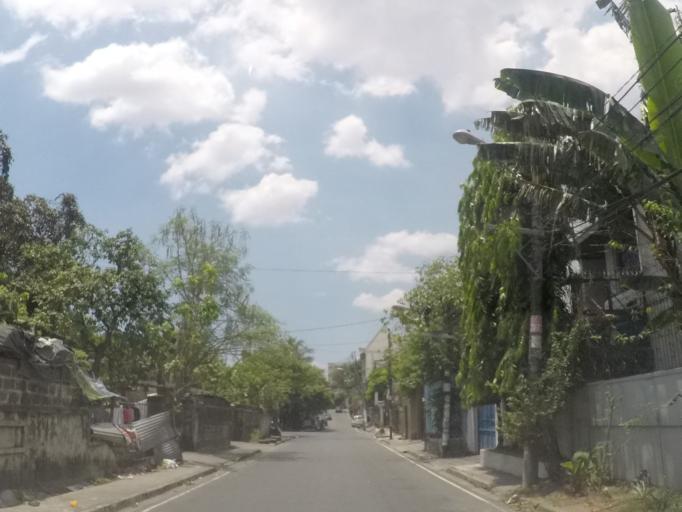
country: PH
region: Metro Manila
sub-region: San Juan
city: San Juan
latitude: 14.6110
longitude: 121.0290
